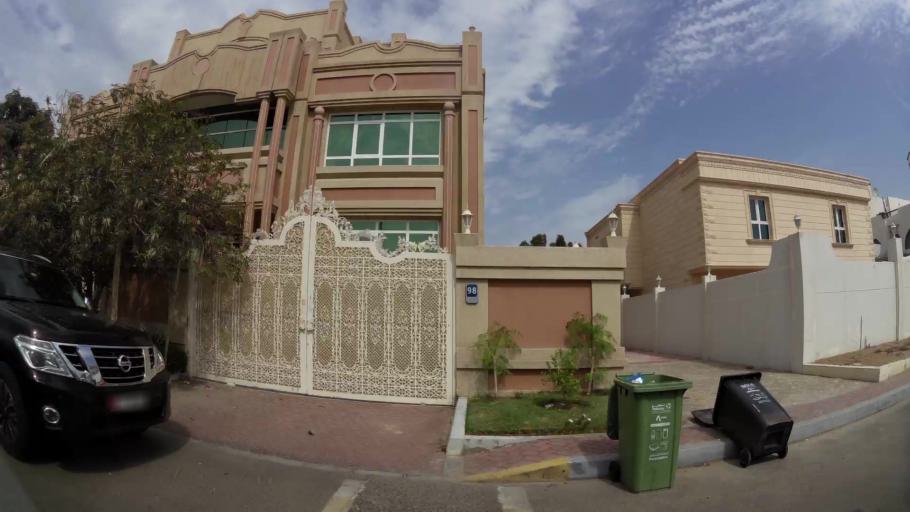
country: AE
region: Abu Dhabi
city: Abu Dhabi
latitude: 24.4617
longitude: 54.3671
